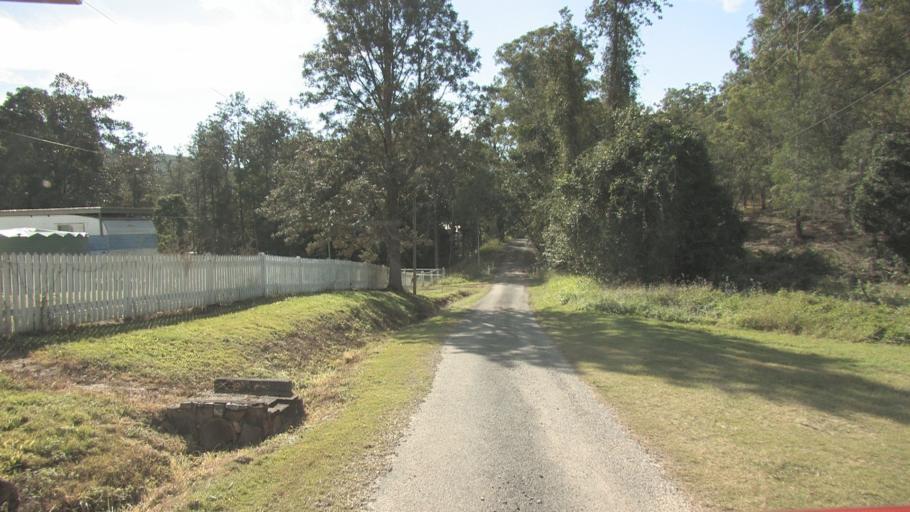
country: AU
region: Queensland
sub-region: Logan
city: Windaroo
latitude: -27.7792
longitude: 153.1739
